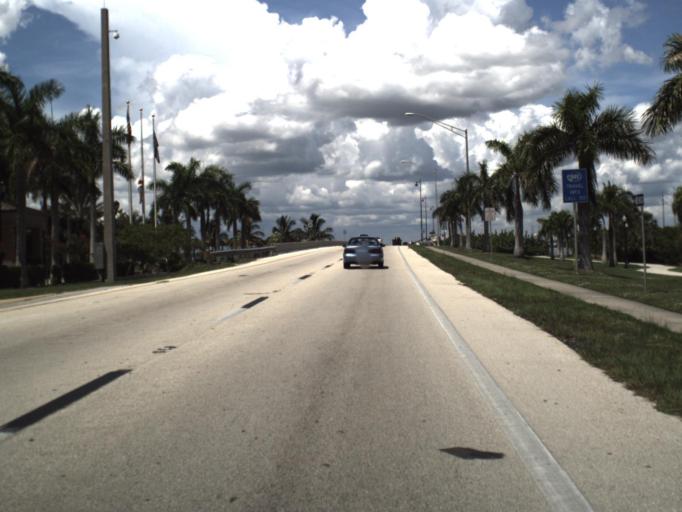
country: US
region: Florida
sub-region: Charlotte County
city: Punta Gorda
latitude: 26.9382
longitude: -82.0519
